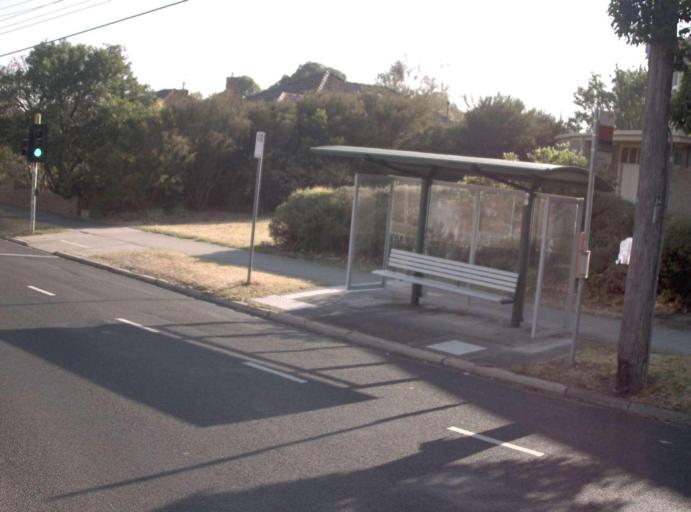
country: AU
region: Victoria
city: Murrumbeena
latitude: -37.9019
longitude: 145.0642
